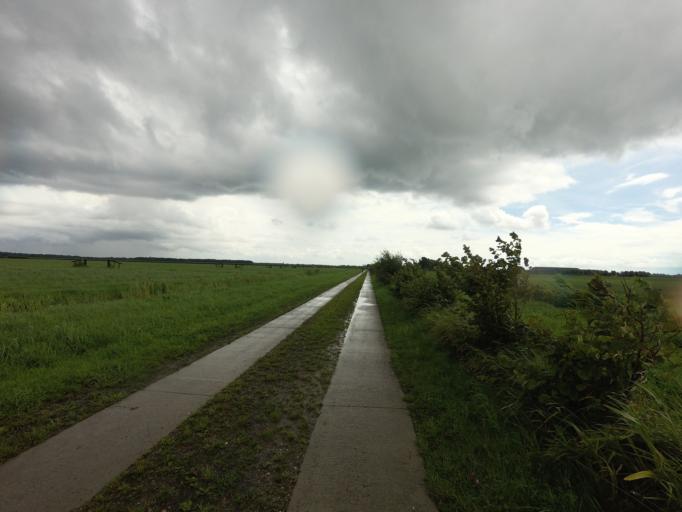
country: NL
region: North Holland
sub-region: Gemeente Wijdemeren
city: Nieuw-Loosdrecht
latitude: 52.1696
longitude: 5.1439
